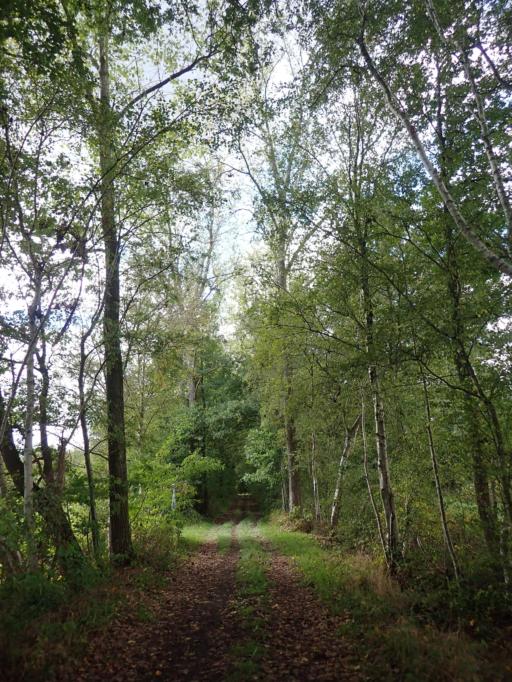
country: BE
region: Flanders
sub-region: Provincie Antwerpen
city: Hulshout
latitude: 51.0875
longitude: 4.7890
